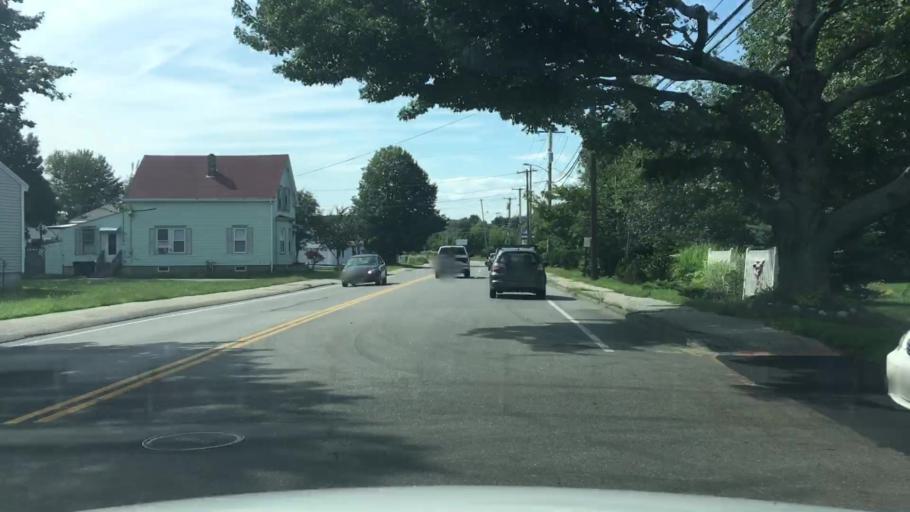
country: US
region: Maine
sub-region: Cumberland County
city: South Portland Gardens
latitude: 43.6301
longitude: -70.2890
